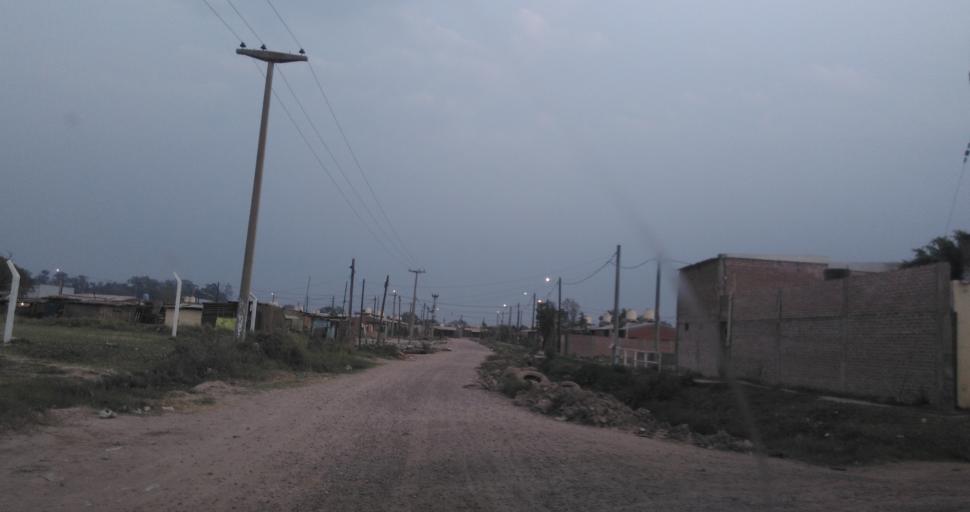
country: AR
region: Chaco
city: Fontana
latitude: -27.4336
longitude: -59.0046
